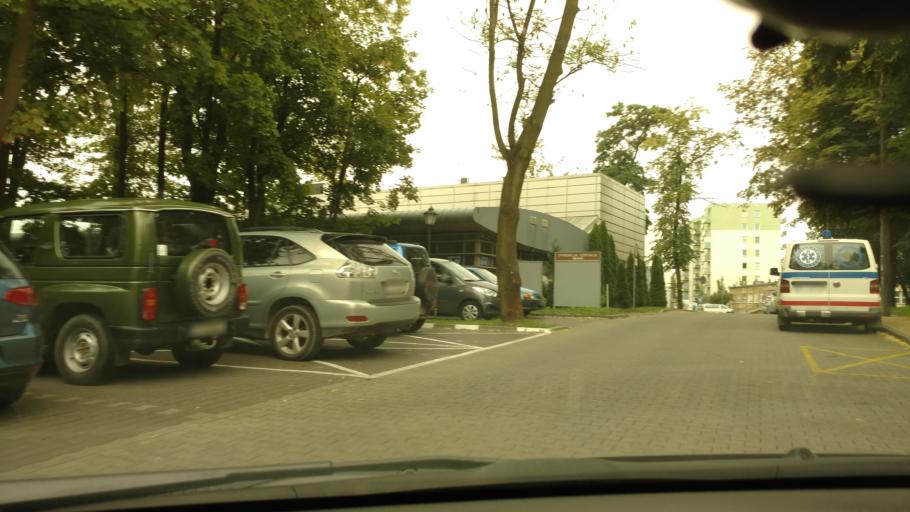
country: PL
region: Lesser Poland Voivodeship
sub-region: Krakow
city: Krakow
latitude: 50.0912
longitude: 19.9351
